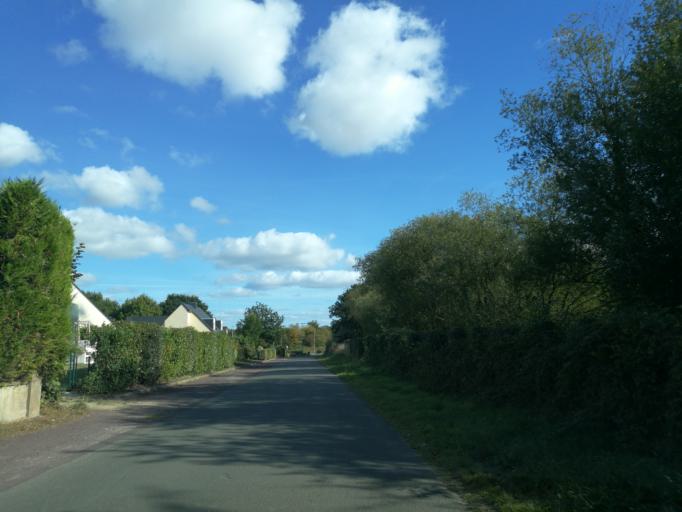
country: FR
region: Brittany
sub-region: Departement d'Ille-et-Vilaine
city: Pleumeleuc
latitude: 48.1801
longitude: -1.9174
